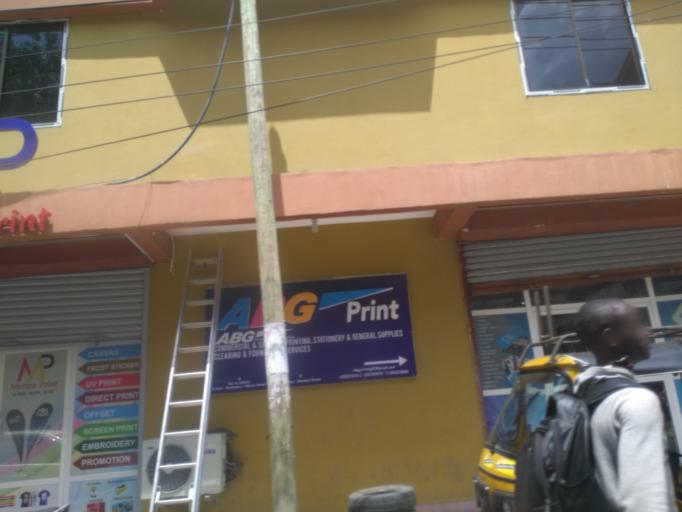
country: TZ
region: Dar es Salaam
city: Dar es Salaam
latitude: -6.8156
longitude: 39.2732
